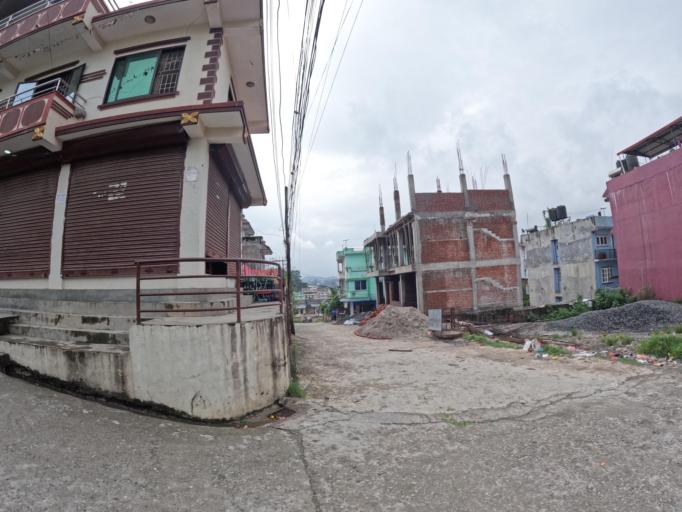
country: NP
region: Central Region
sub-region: Bagmati Zone
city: Kathmandu
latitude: 27.7578
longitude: 85.3226
